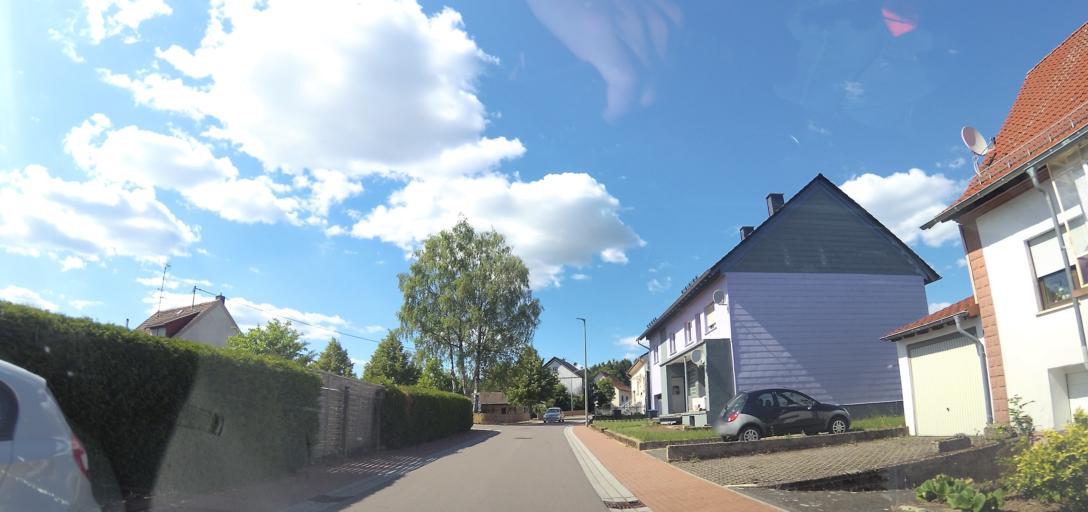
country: DE
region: Saarland
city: Weiskirchen
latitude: 49.5570
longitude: 6.8302
